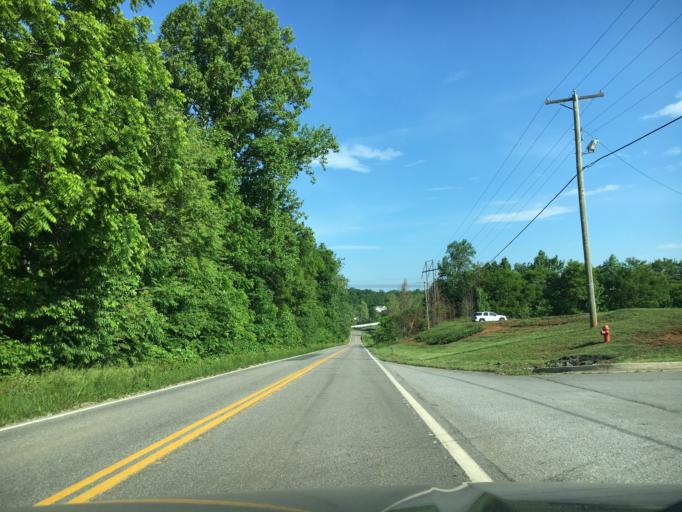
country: US
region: Virginia
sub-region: Campbell County
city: Rustburg
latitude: 37.3092
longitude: -79.1696
